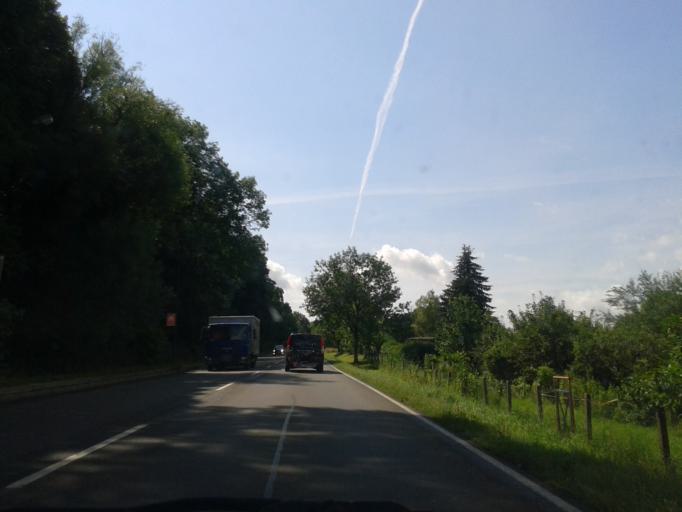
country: DE
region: Mecklenburg-Vorpommern
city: Pasewalk
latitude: 53.4948
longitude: 13.9835
